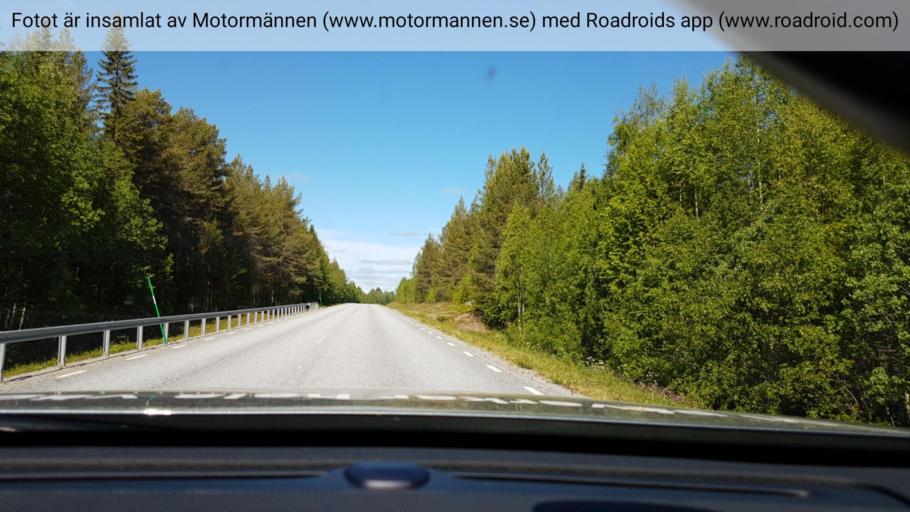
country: SE
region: Vaesterbotten
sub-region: Vilhelmina Kommun
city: Vilhelmina
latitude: 64.3916
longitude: 16.8712
